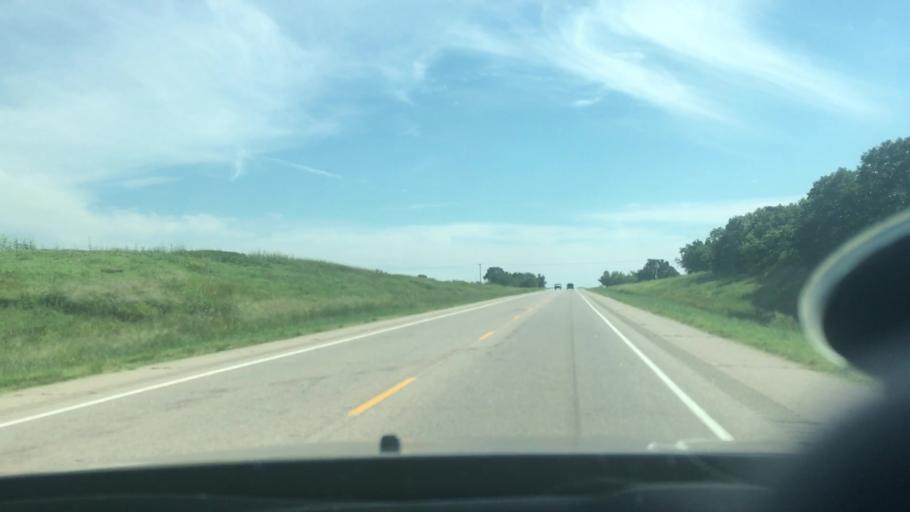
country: US
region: Oklahoma
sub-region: Seminole County
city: Maud
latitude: 35.0974
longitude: -96.6788
